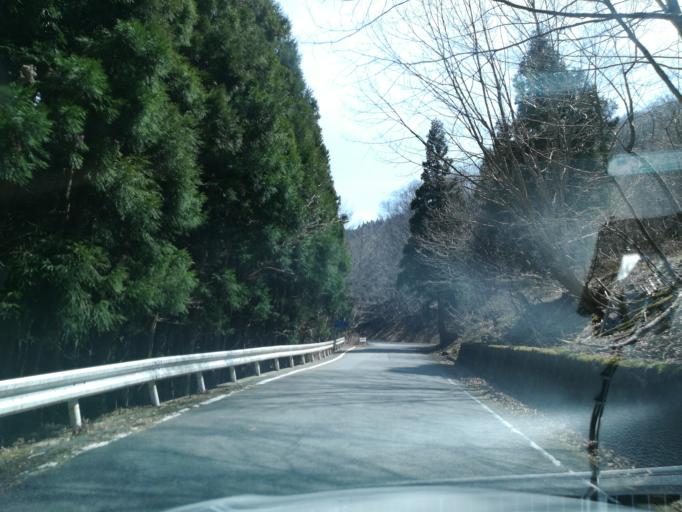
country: JP
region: Tokushima
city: Wakimachi
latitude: 33.8838
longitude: 134.0508
